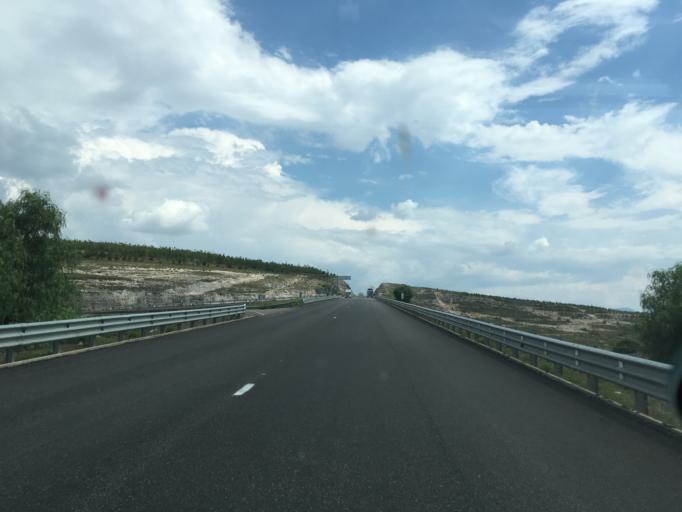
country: MX
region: Oaxaca
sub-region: Villa Tejupam de la Union
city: Villa Tejupam de la Union
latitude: 17.8677
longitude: -97.3764
